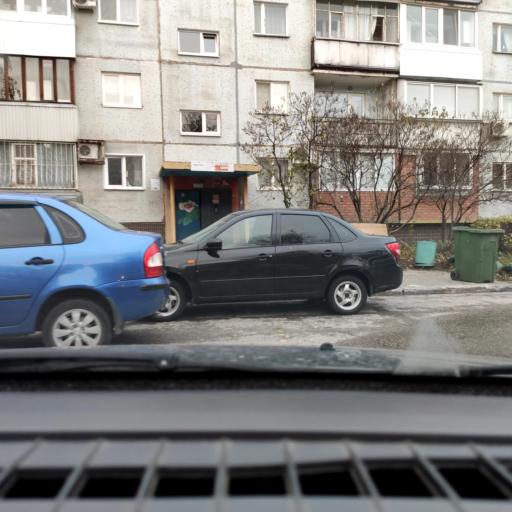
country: RU
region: Samara
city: Tol'yatti
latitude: 53.5307
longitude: 49.2706
